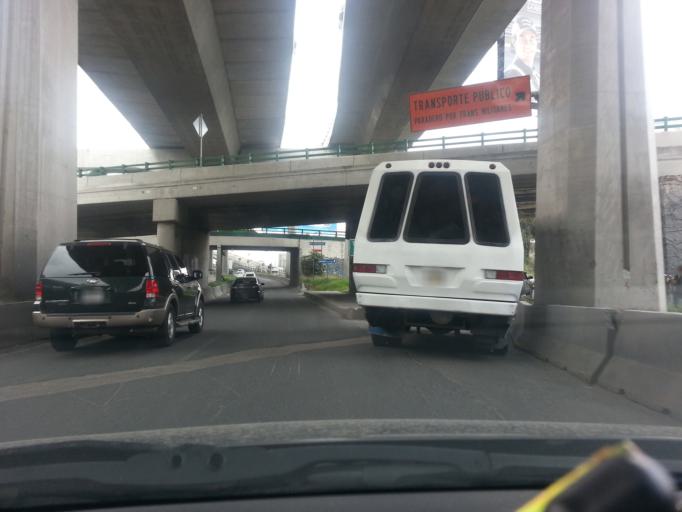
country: MX
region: Mexico City
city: Miguel Hidalgo
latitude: 19.4560
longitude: -99.2198
